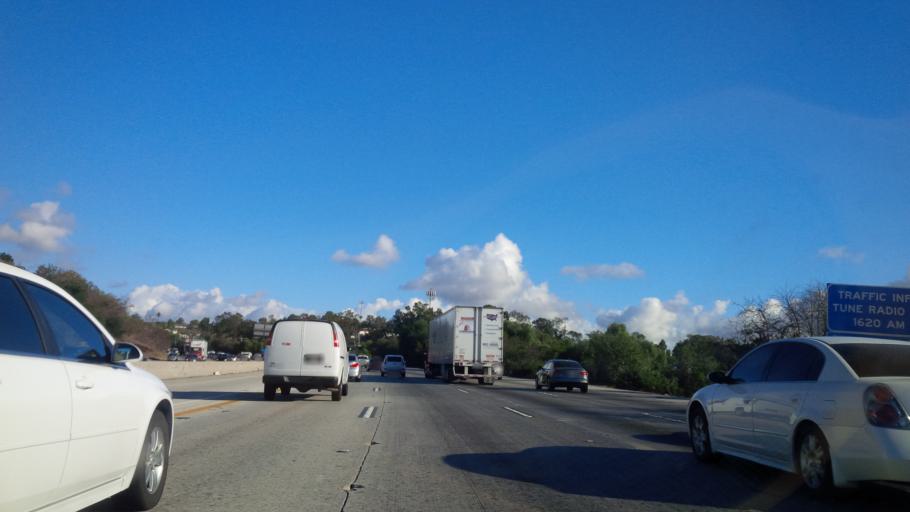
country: US
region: California
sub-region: Los Angeles County
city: Walnut
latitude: 33.9770
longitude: -117.8423
